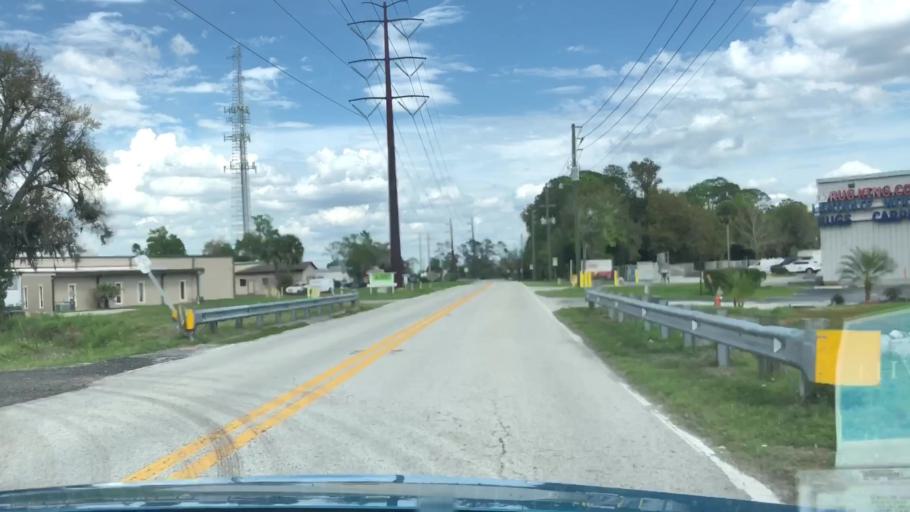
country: US
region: Florida
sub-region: Seminole County
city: Lake Mary
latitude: 28.8149
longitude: -81.3332
